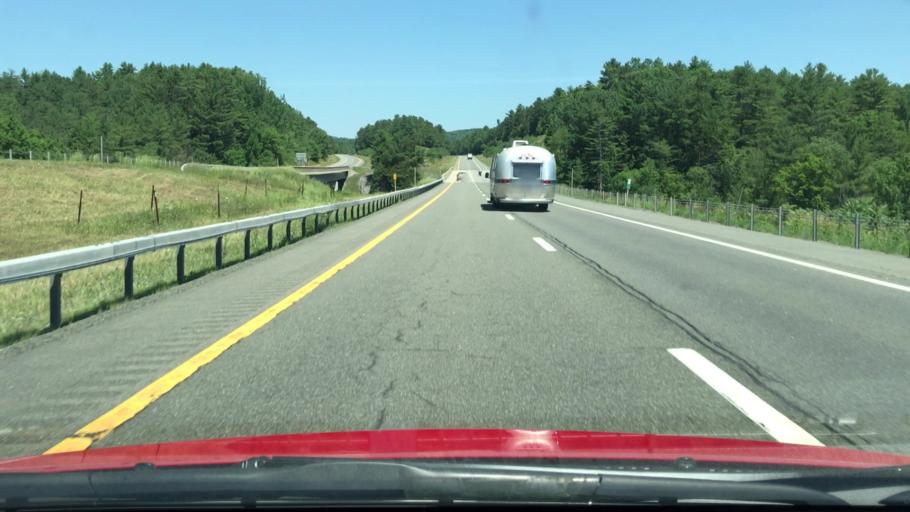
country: US
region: New York
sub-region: Essex County
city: Elizabethtown
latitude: 44.3068
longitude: -73.5299
